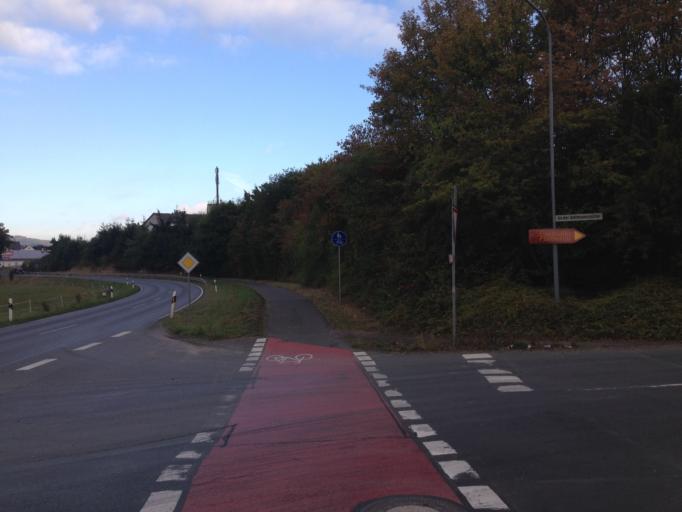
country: DE
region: Hesse
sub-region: Regierungsbezirk Giessen
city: Heuchelheim
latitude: 50.6121
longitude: 8.6125
